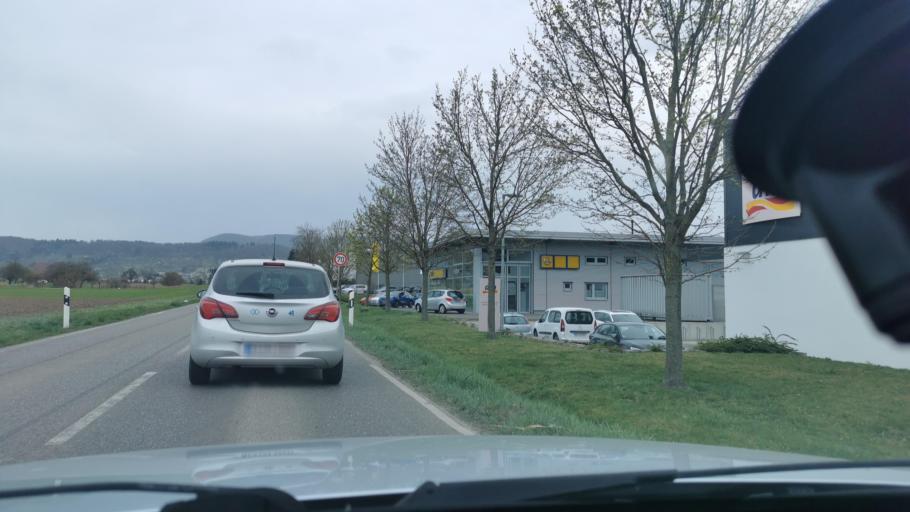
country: DE
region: Baden-Wuerttemberg
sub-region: Regierungsbezirk Stuttgart
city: Holzmaden
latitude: 48.6254
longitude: 9.5275
